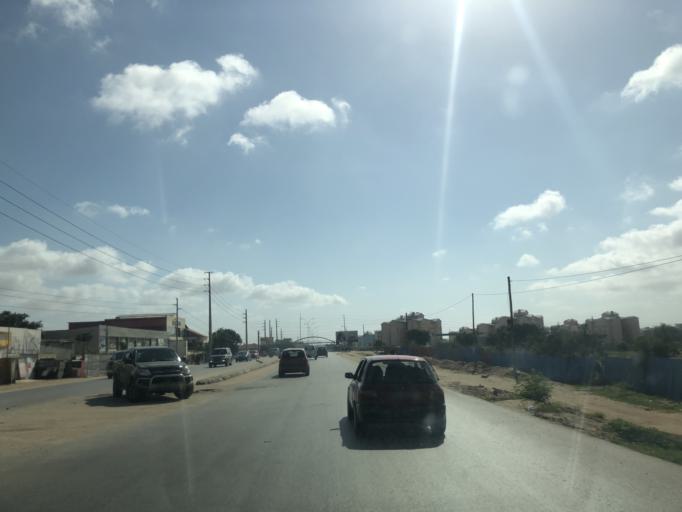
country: AO
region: Luanda
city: Luanda
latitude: -8.9110
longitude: 13.2372
